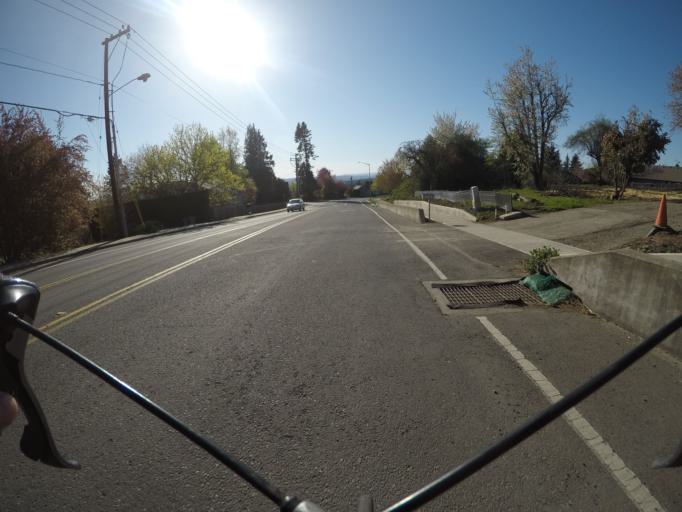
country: US
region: Oregon
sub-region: Washington County
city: King City
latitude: 45.4160
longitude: -122.8351
